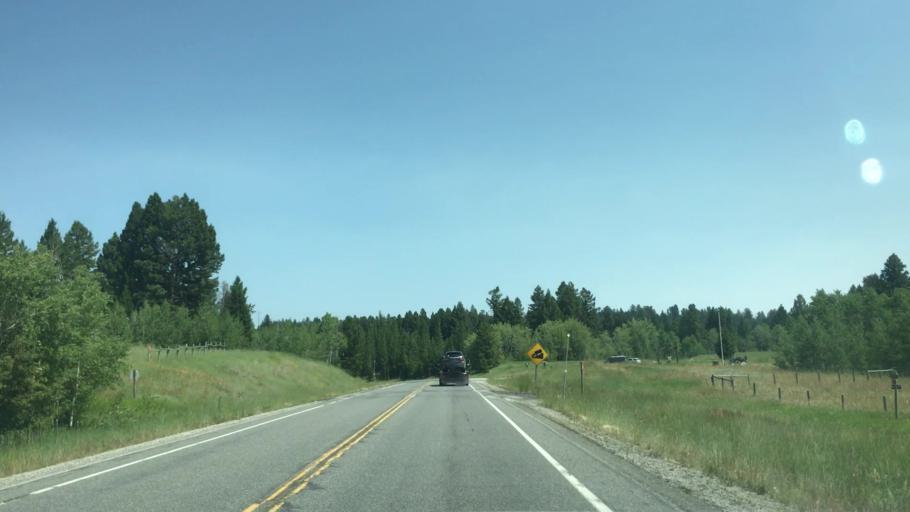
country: US
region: Montana
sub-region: Gallatin County
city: West Yellowstone
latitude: 44.7949
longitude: -111.1058
